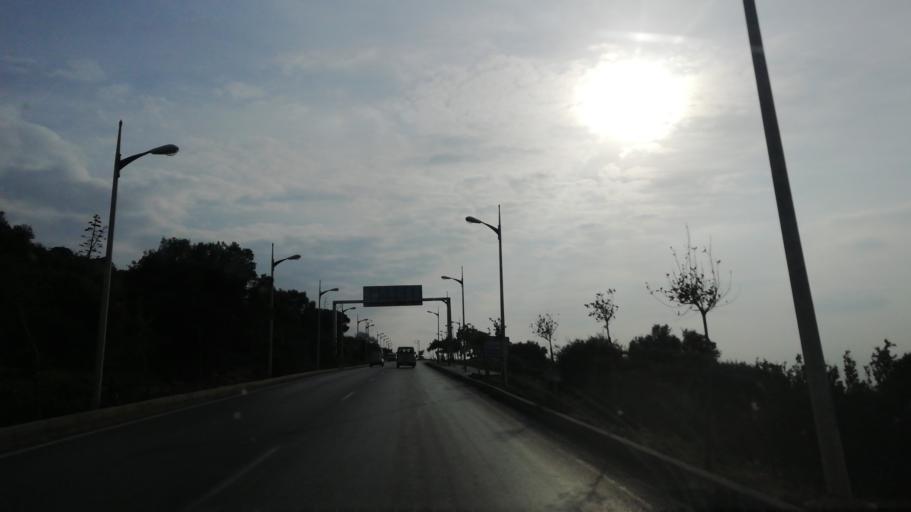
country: DZ
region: Mostaganem
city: Mostaganem
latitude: 35.9095
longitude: 0.0787
